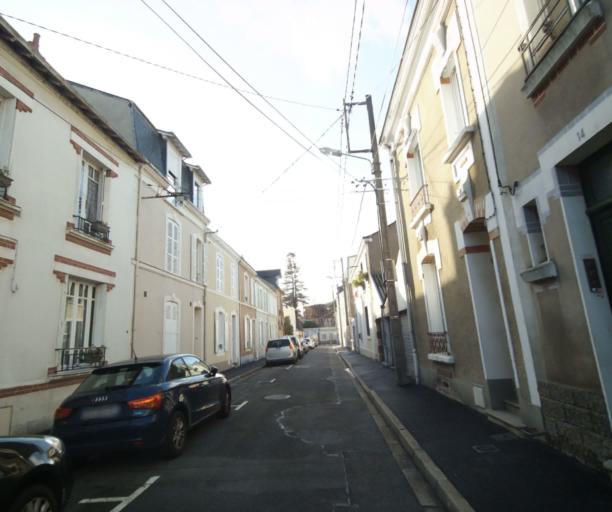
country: FR
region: Pays de la Loire
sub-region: Departement de la Sarthe
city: Le Mans
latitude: 48.0088
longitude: 0.1843
